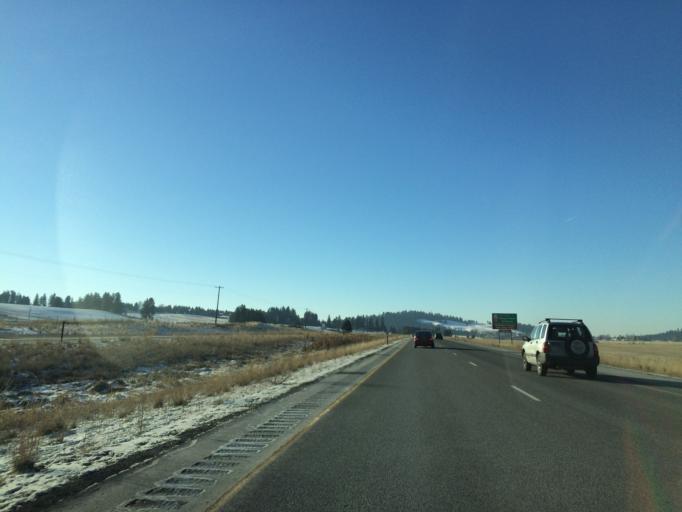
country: US
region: Washington
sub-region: Spokane County
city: Airway Heights
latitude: 47.5754
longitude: -117.5829
